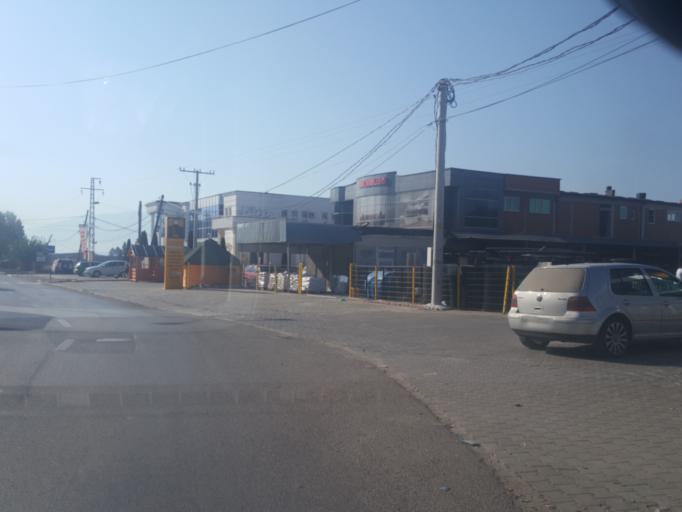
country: XK
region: Gjakova
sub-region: Komuna e Gjakoves
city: Gjakove
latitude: 42.3979
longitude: 20.4186
